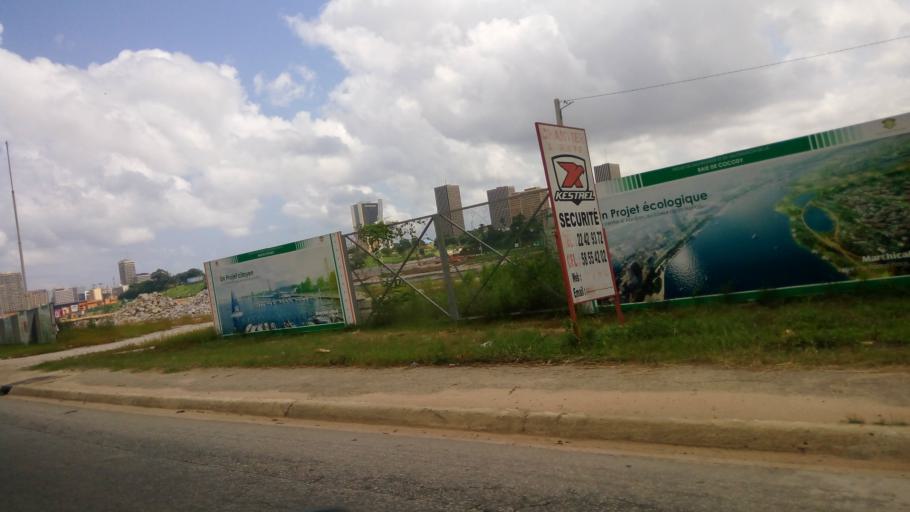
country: CI
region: Lagunes
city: Abidjan
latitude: 5.3390
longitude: -4.0137
